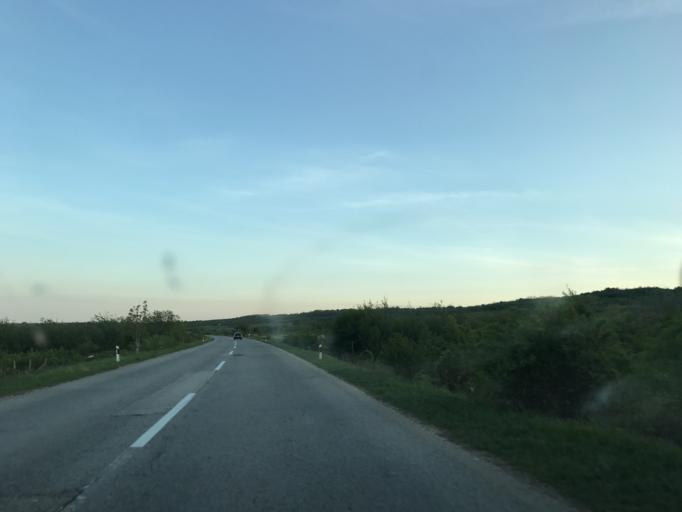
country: RO
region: Mehedinti
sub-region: Comuna Gogosu
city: Ostrovu Mare
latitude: 44.3398
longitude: 22.4736
